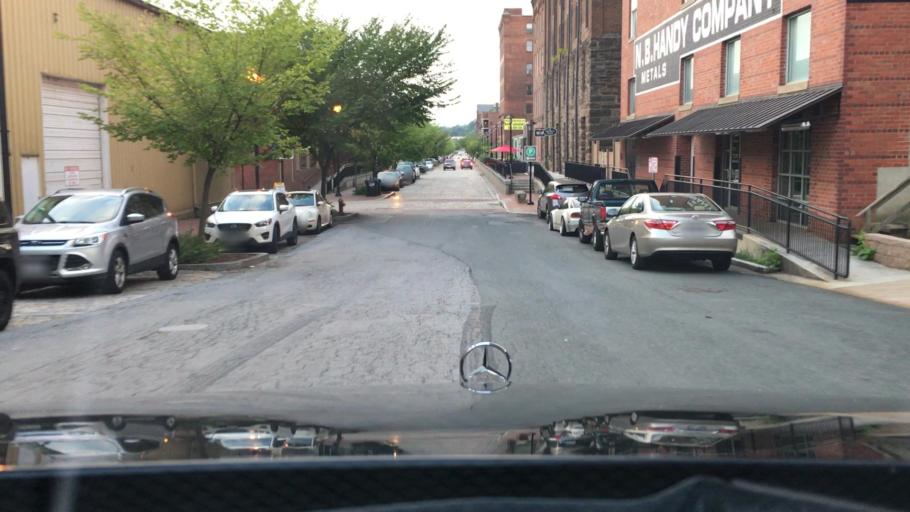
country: US
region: Virginia
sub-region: City of Lynchburg
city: Lynchburg
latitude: 37.4154
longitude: -79.1400
